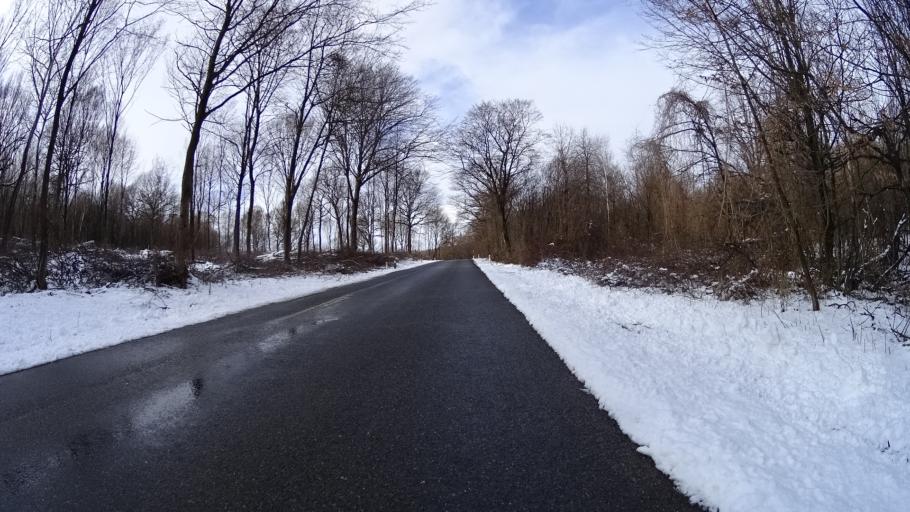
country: AT
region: Lower Austria
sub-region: Politischer Bezirk Korneuburg
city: Leobendorf
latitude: 48.4164
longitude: 16.3391
